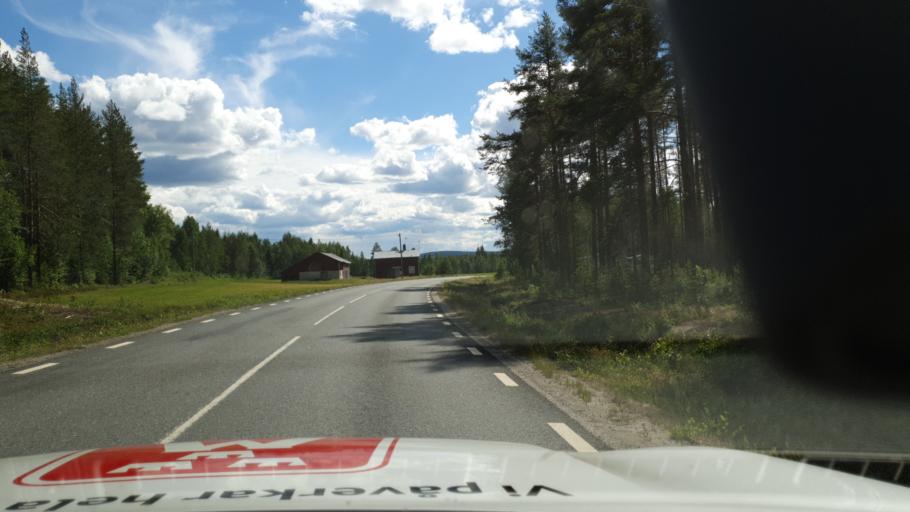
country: SE
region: Vaesterbotten
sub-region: Bjurholms Kommun
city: Bjurholm
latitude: 64.3471
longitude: 19.1498
